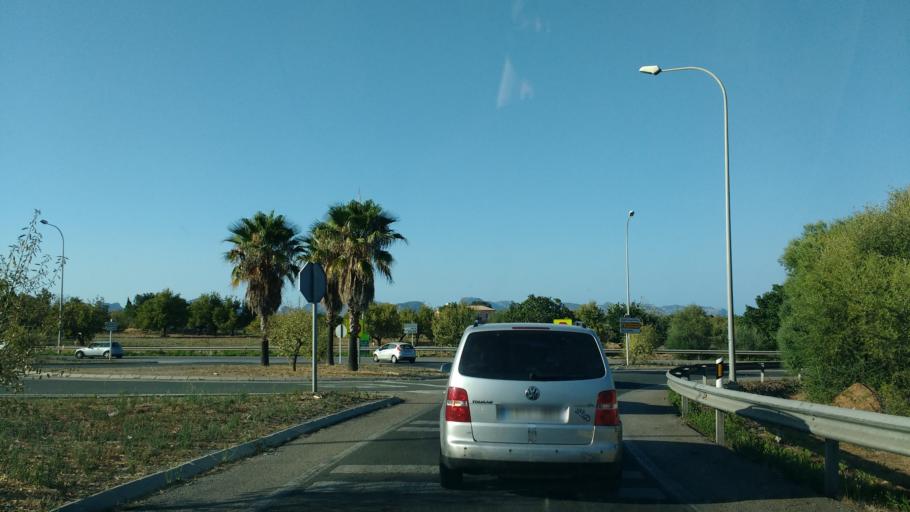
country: ES
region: Balearic Islands
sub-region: Illes Balears
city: Alcudia
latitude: 39.8423
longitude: 3.0979
